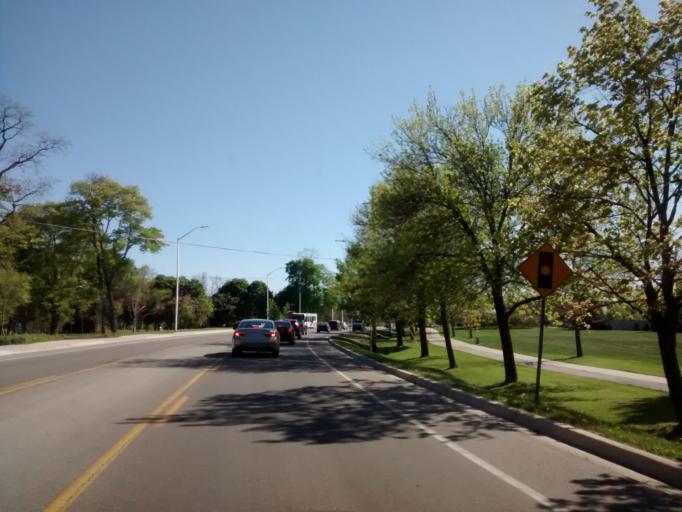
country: CA
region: Ontario
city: Oakville
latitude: 43.3779
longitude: -79.7177
